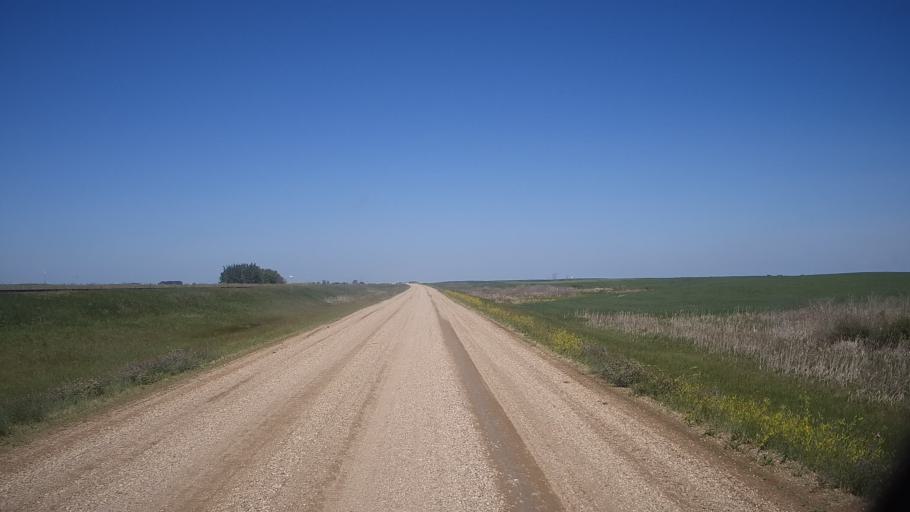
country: CA
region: Saskatchewan
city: Watrous
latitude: 51.8443
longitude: -105.9169
